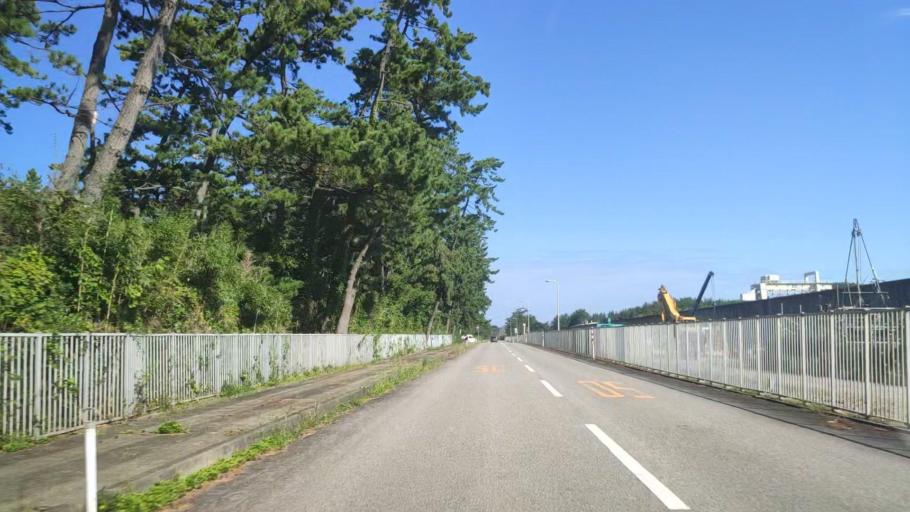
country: JP
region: Ishikawa
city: Hakui
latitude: 37.0593
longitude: 136.7237
